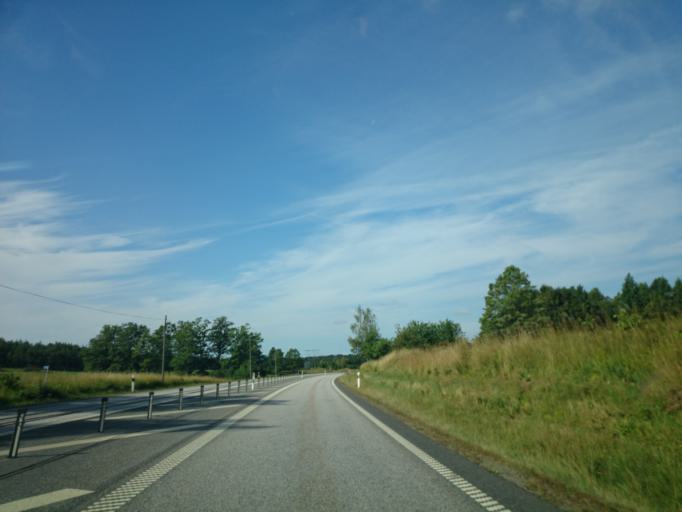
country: SE
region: Kalmar
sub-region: Vasterviks Kommun
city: Gamleby
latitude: 57.9382
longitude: 16.4222
